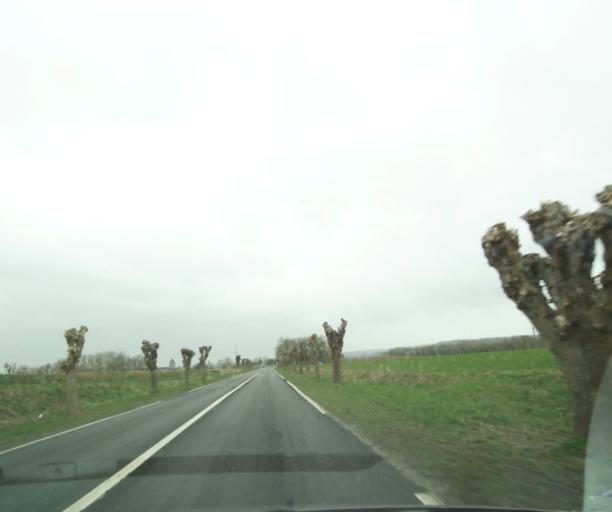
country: FR
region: Picardie
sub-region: Departement de l'Oise
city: Noyon
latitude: 49.5959
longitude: 3.0066
